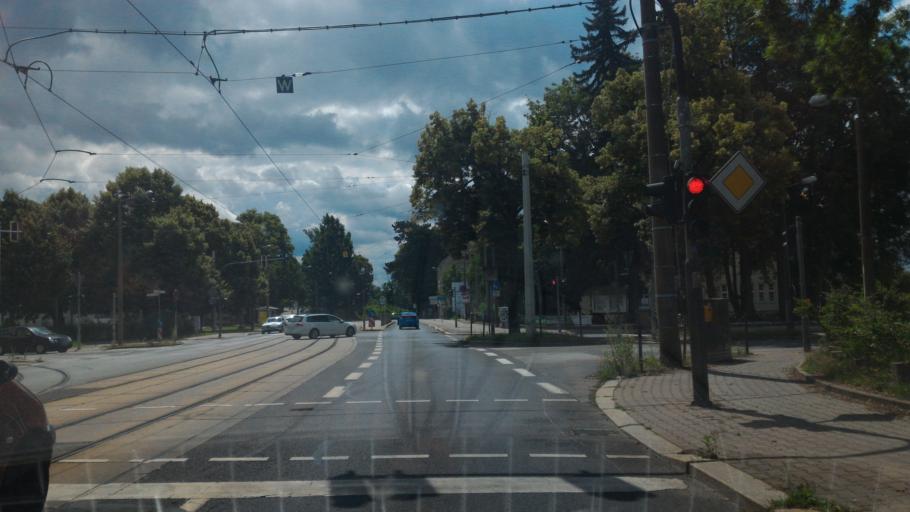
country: DE
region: Saxony
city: Goerlitz
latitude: 51.1393
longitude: 14.9797
